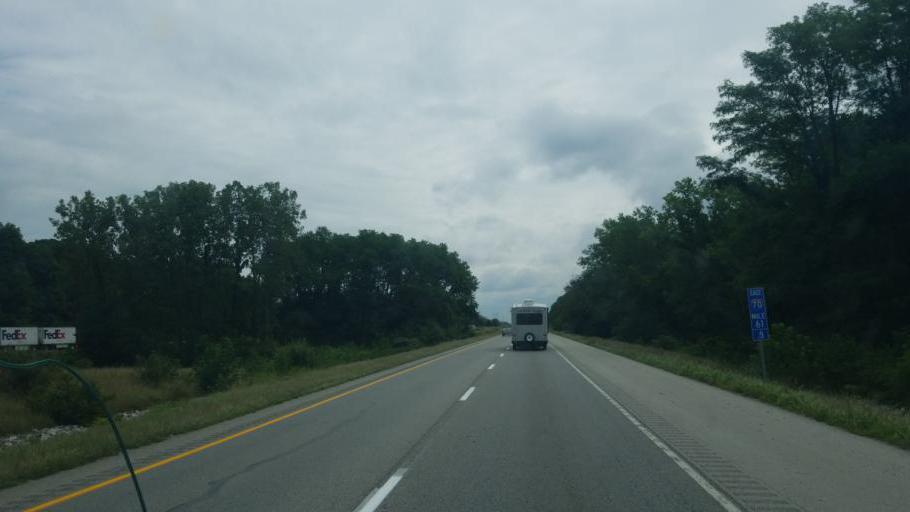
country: US
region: Indiana
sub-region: Morgan County
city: Monrovia
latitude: 39.6318
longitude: -86.4427
